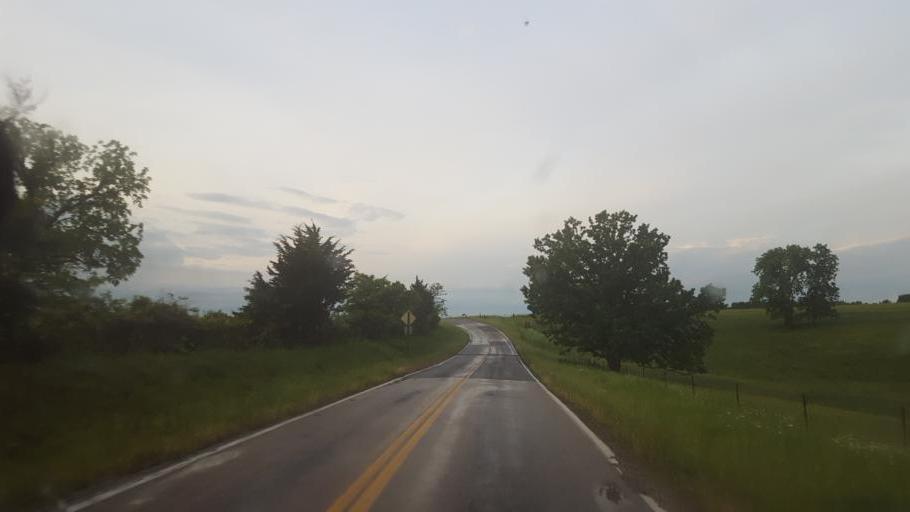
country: US
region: Missouri
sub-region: Moniteau County
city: California
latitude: 38.7228
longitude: -92.6356
